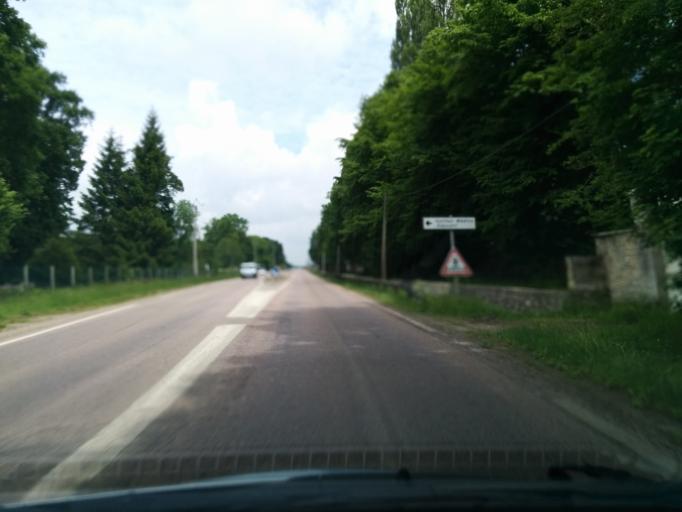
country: FR
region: Haute-Normandie
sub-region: Departement de l'Eure
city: Vernon
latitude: 49.1305
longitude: 1.5155
